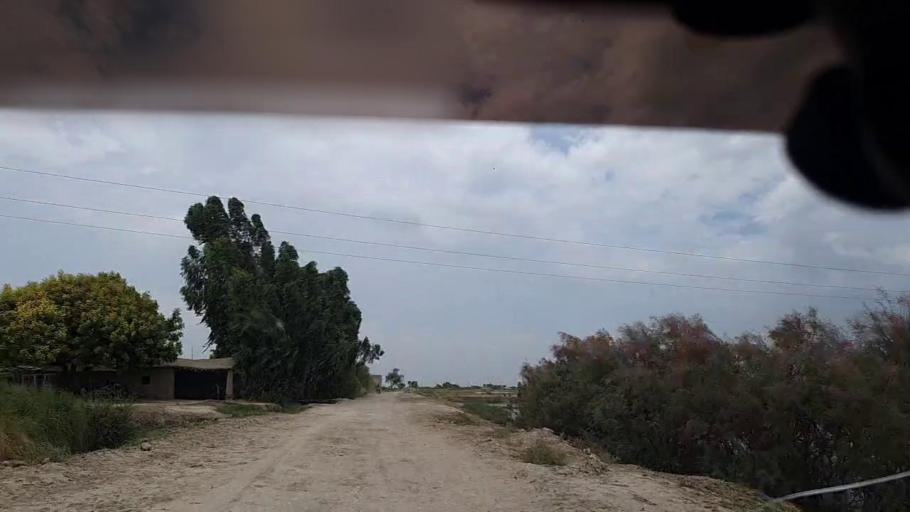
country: PK
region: Sindh
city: Ghauspur
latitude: 28.1111
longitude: 68.9860
